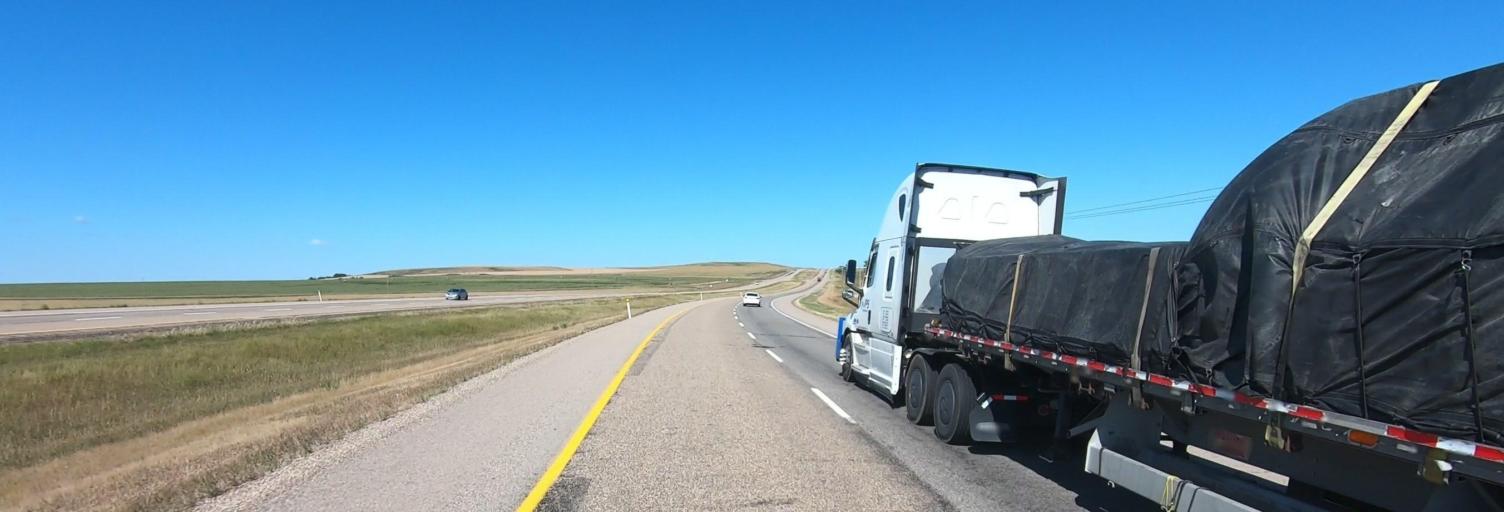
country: CA
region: Alberta
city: Bassano
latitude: 50.8356
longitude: -112.8140
